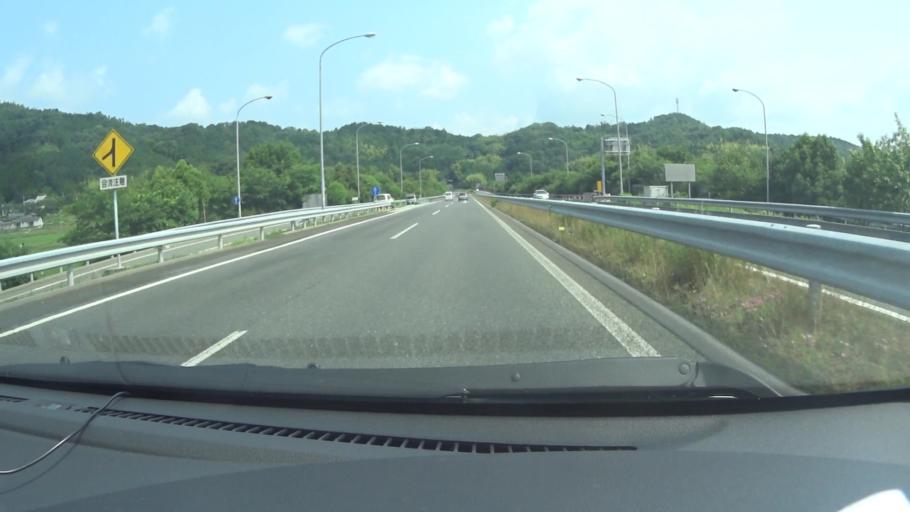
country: JP
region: Kyoto
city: Kameoka
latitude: 35.0522
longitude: 135.5346
